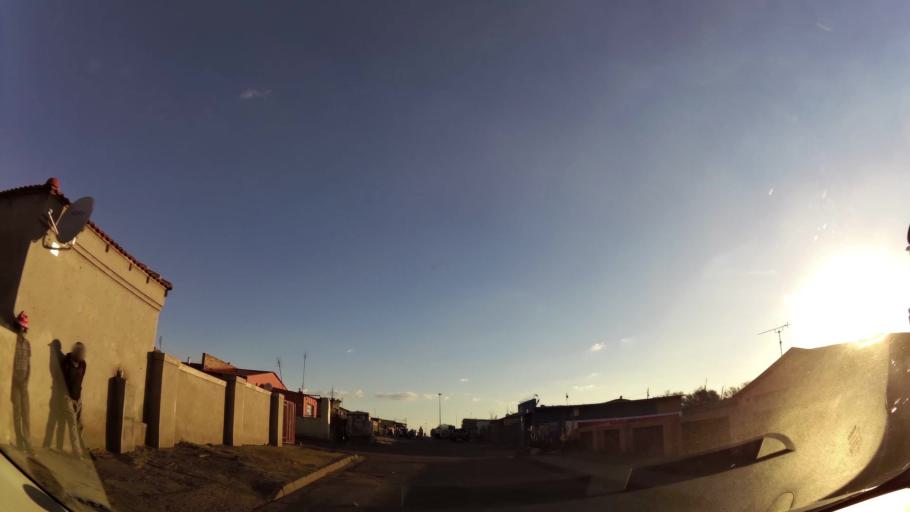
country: ZA
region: Mpumalanga
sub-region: Nkangala District Municipality
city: Witbank
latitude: -25.8779
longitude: 29.1941
